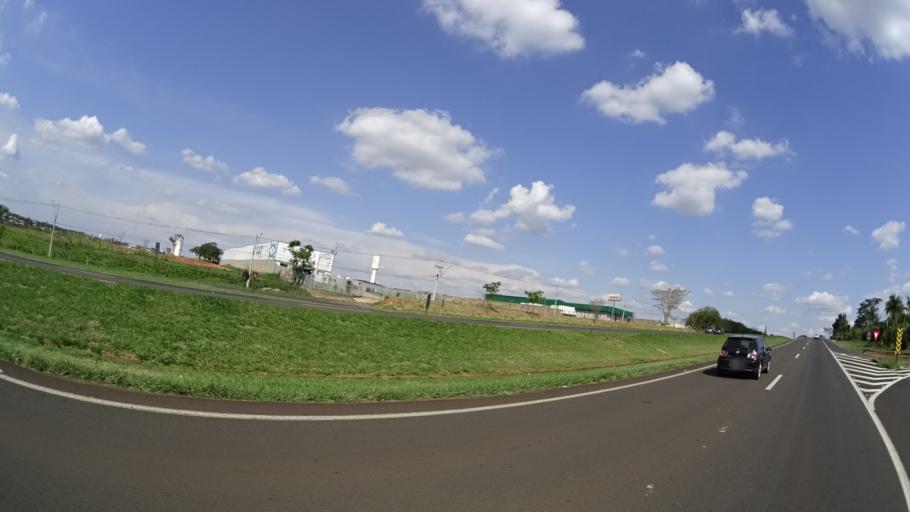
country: BR
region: Sao Paulo
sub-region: Sao Jose Do Rio Preto
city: Sao Jose do Rio Preto
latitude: -20.8635
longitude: -49.3332
